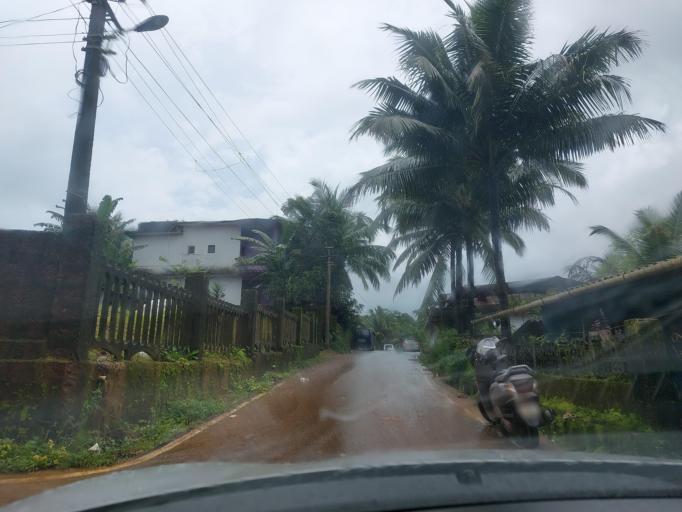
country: IN
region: Goa
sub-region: North Goa
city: Valpoy
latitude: 15.5331
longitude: 74.1301
